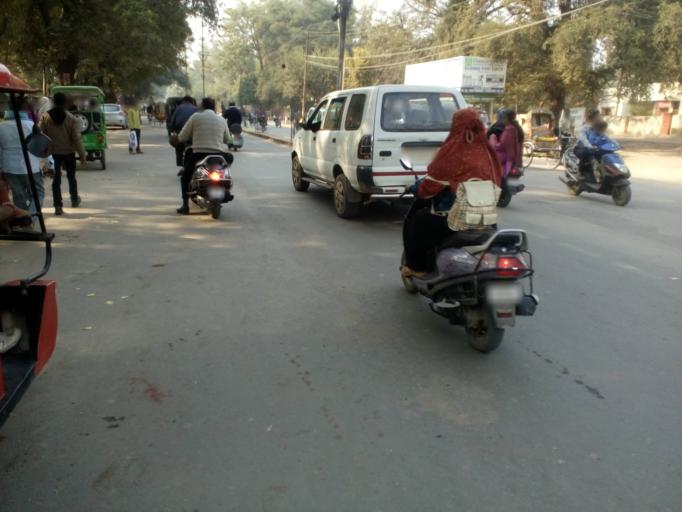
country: IN
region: Uttar Pradesh
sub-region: Allahabad
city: Allahabad
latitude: 25.4481
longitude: 81.8478
